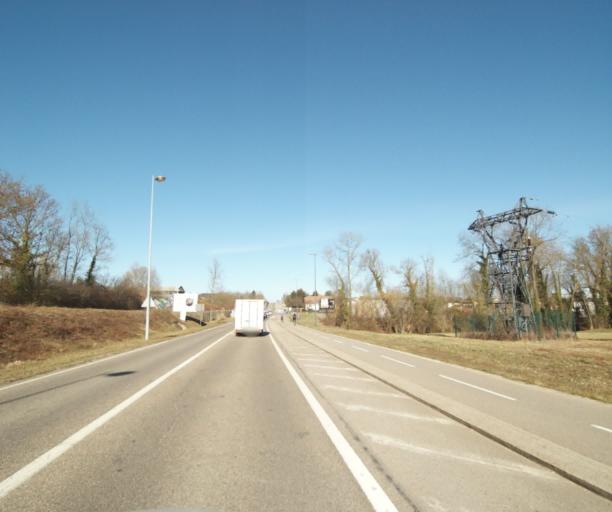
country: FR
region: Lorraine
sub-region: Departement de Meurthe-et-Moselle
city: Vandoeuvre-les-Nancy
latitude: 48.6487
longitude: 6.1828
